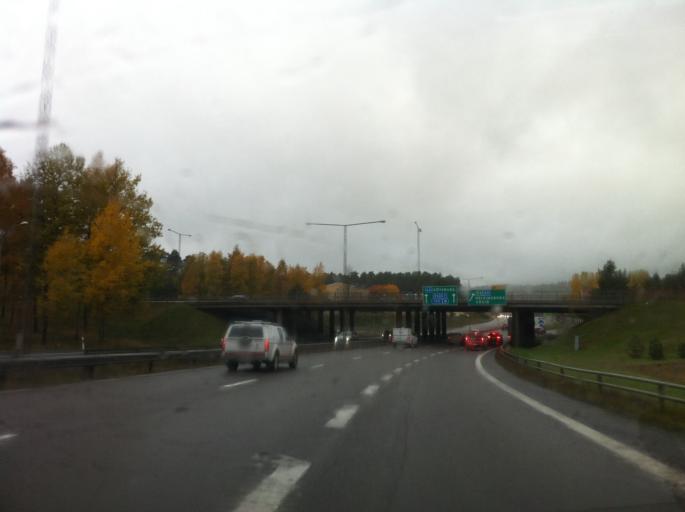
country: SE
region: Joenkoeping
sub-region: Jonkopings Kommun
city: Jonkoping
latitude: 57.7595
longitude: 14.1717
